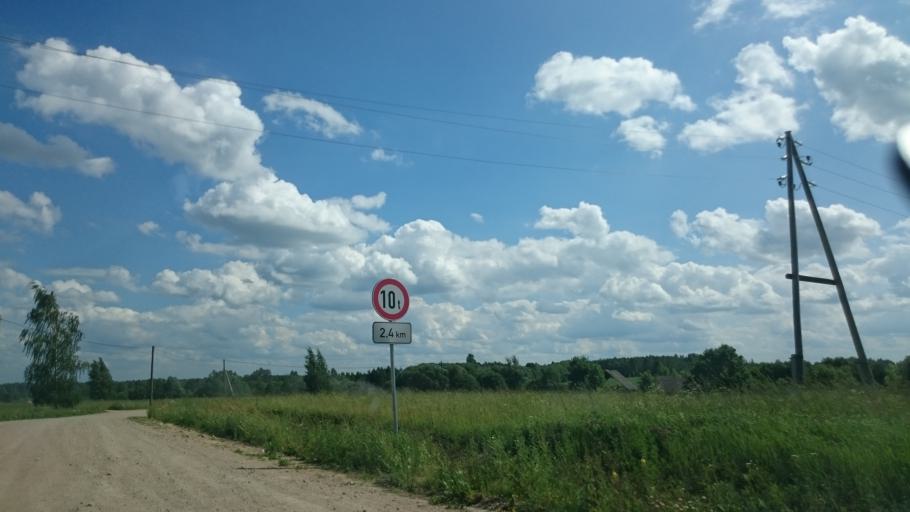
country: LV
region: Ludzas Rajons
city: Ludza
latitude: 56.6022
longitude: 27.7867
